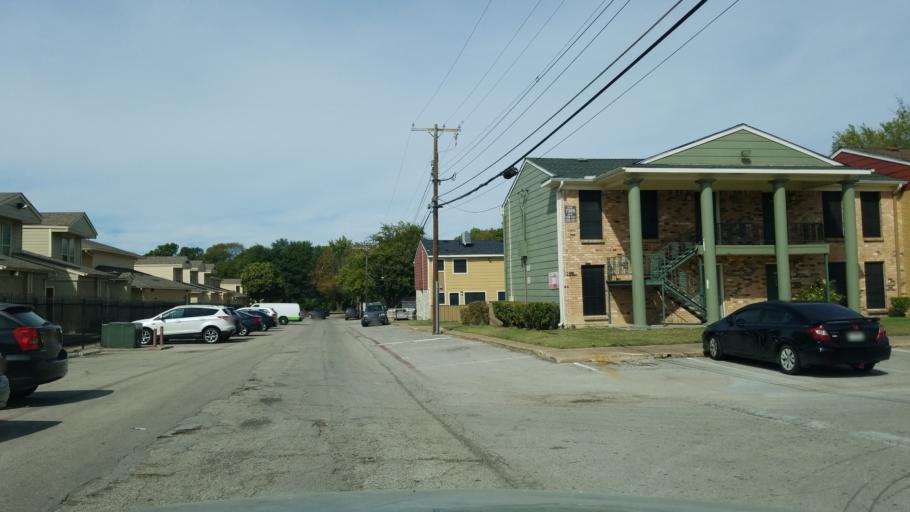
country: US
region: Texas
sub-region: Dallas County
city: Highland Park
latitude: 32.7972
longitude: -96.7218
